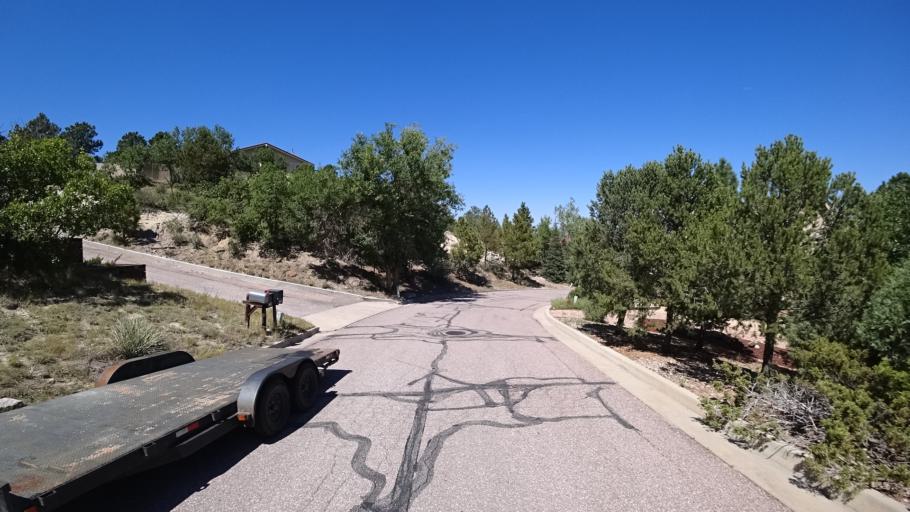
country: US
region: Colorado
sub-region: El Paso County
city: Colorado Springs
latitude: 38.9214
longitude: -104.8068
